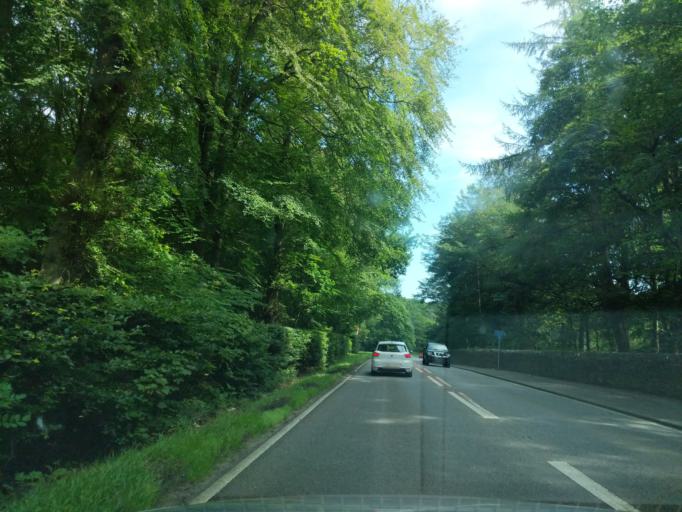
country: GB
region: Scotland
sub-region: Angus
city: Muirhead
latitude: 56.4877
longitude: -3.0383
